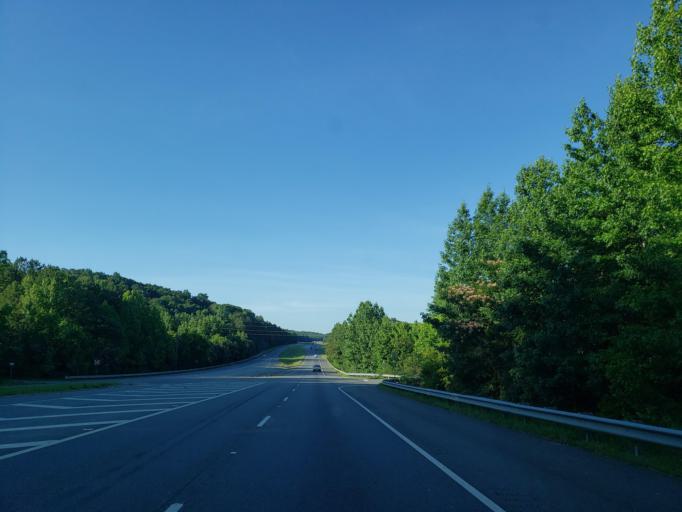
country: US
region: Georgia
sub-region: Floyd County
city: Shannon
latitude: 34.3155
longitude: -85.1076
